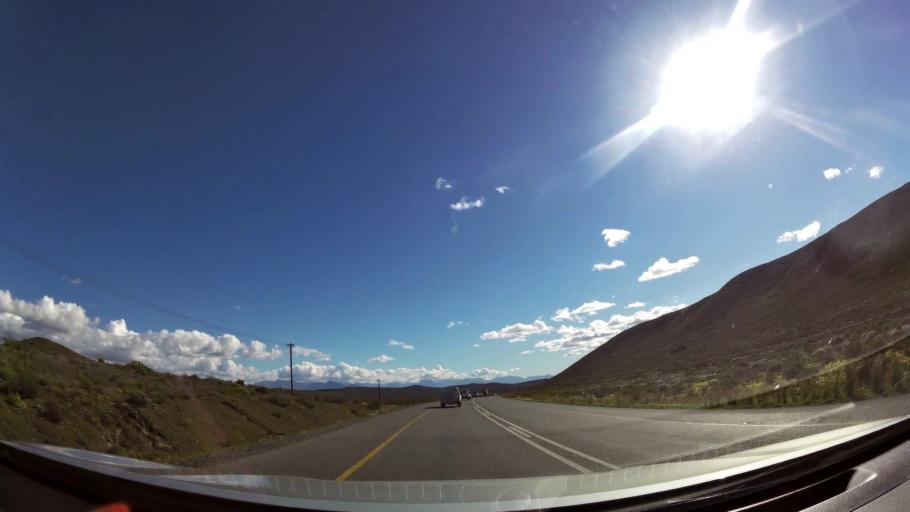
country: ZA
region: Western Cape
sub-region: Cape Winelands District Municipality
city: Worcester
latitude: -33.7348
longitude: 19.6552
